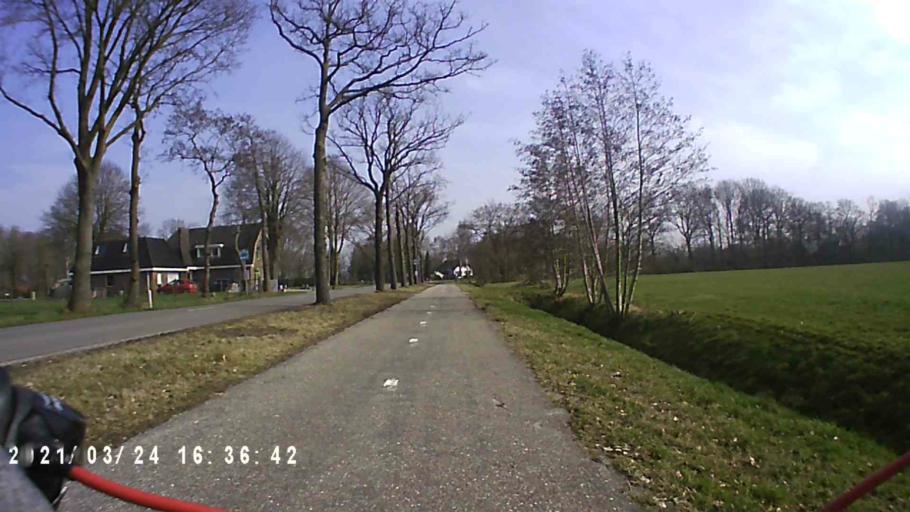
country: NL
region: Groningen
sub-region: Gemeente Leek
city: Leek
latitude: 53.0637
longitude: 6.2803
